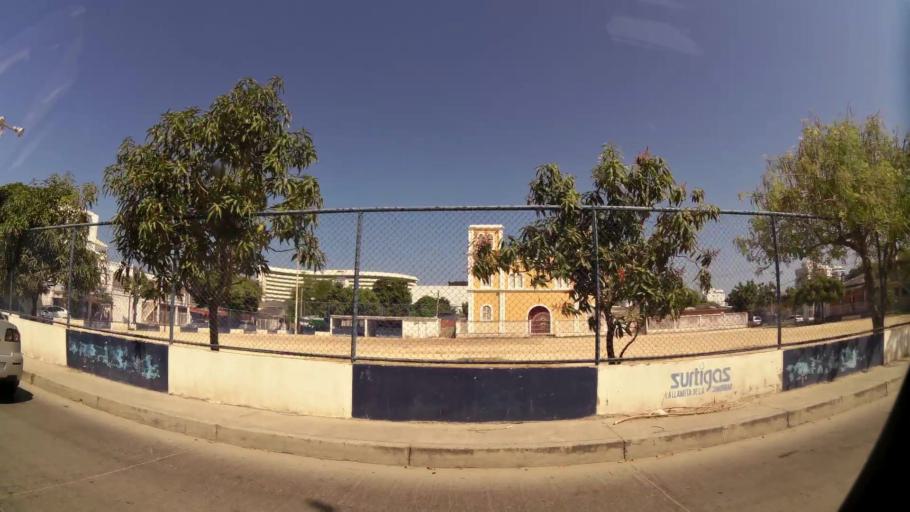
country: CO
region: Bolivar
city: Cartagena
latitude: 10.4401
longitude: -75.5245
